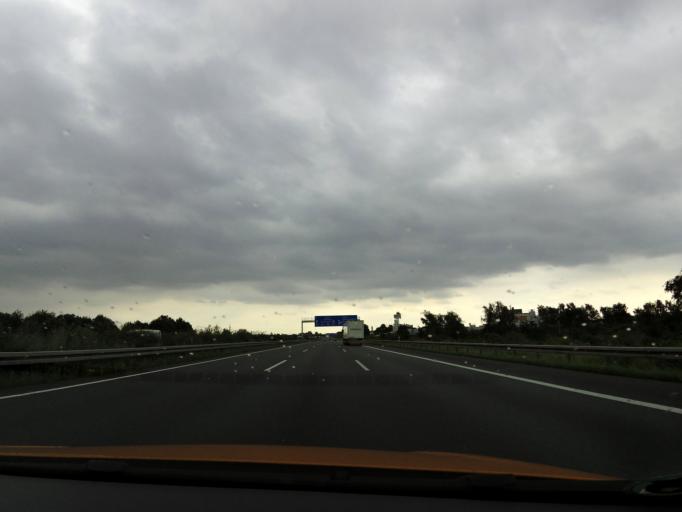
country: DE
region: Lower Saxony
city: Vordorf
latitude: 52.3206
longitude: 10.4914
